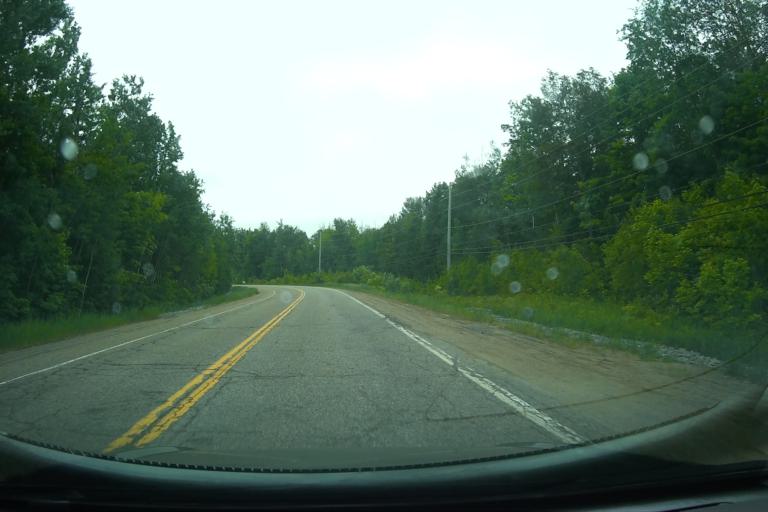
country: CA
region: Ontario
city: Pembroke
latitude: 45.4531
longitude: -77.2949
